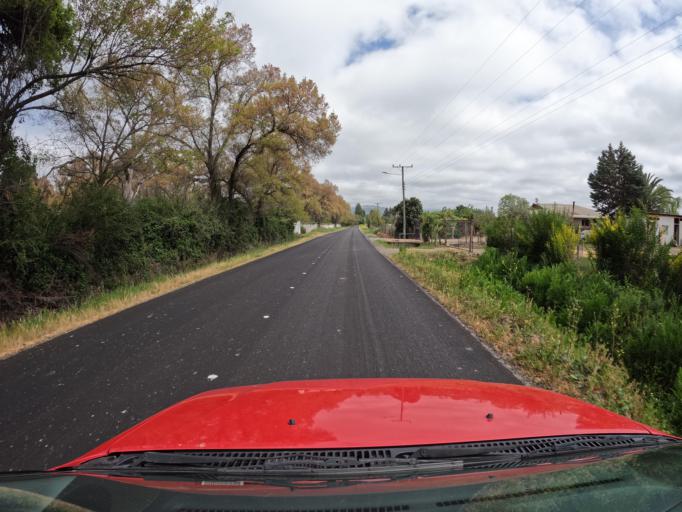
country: CL
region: O'Higgins
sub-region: Provincia de Colchagua
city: Santa Cruz
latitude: -34.6727
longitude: -71.3777
